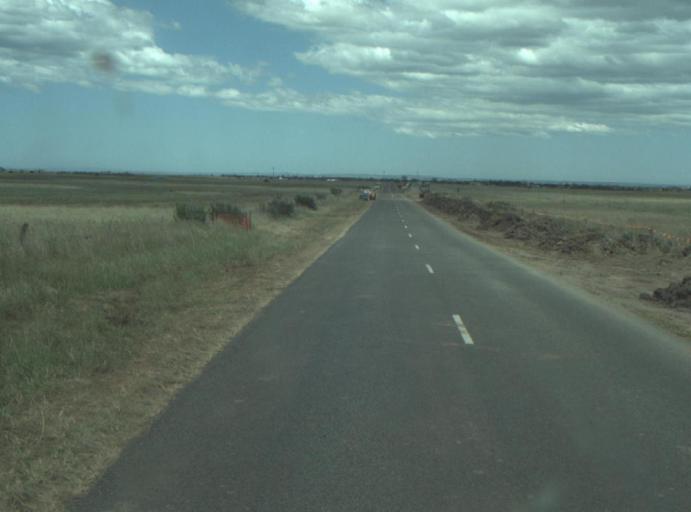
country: AU
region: Victoria
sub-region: Wyndham
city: Little River
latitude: -37.8901
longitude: 144.4611
